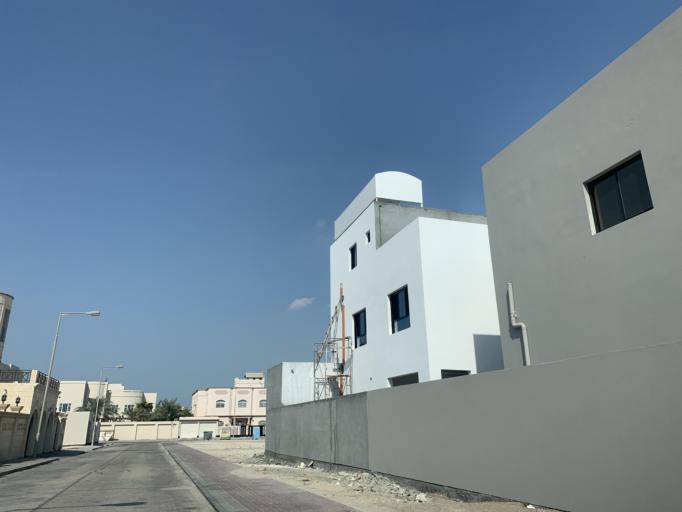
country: BH
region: Central Governorate
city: Madinat Hamad
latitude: 26.1286
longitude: 50.5050
